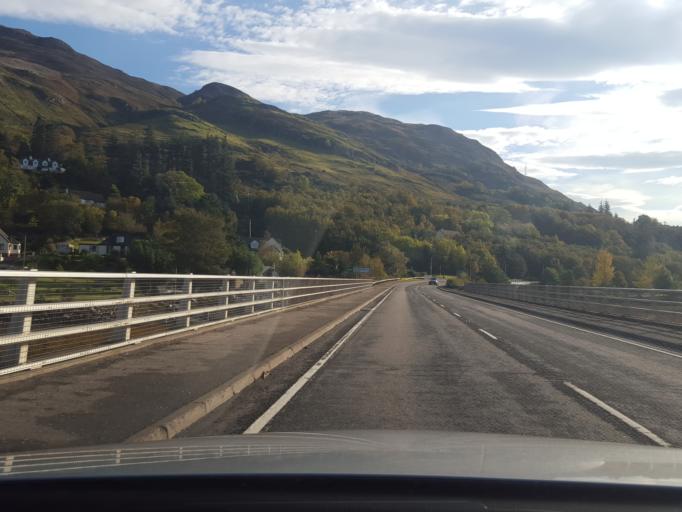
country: GB
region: Scotland
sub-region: Highland
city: Fort William
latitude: 57.2776
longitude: -5.5170
